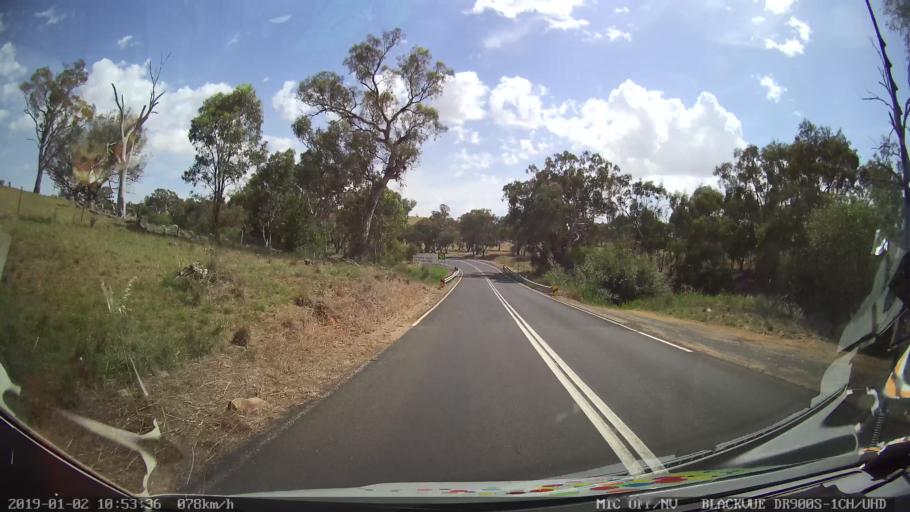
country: AU
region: New South Wales
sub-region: Cootamundra
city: Cootamundra
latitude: -34.6767
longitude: 148.2773
